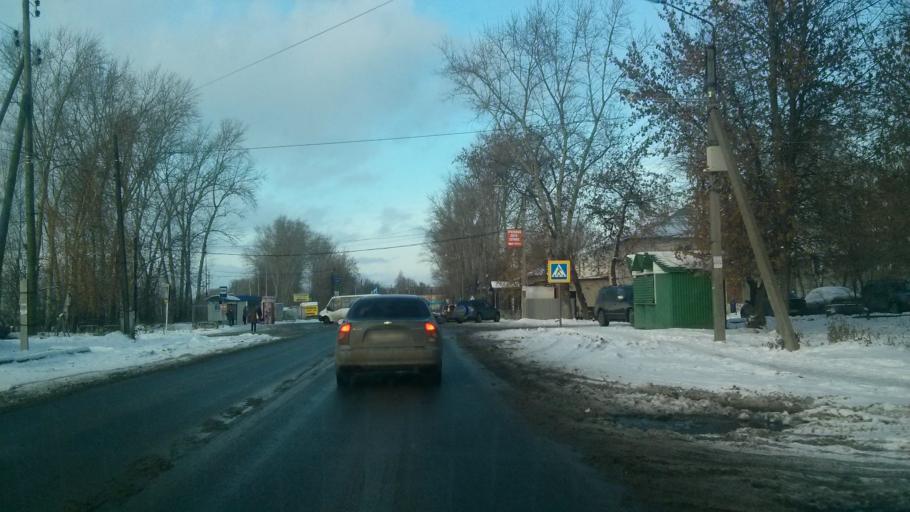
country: RU
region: Vladimir
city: Murom
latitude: 55.5949
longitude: 42.0342
